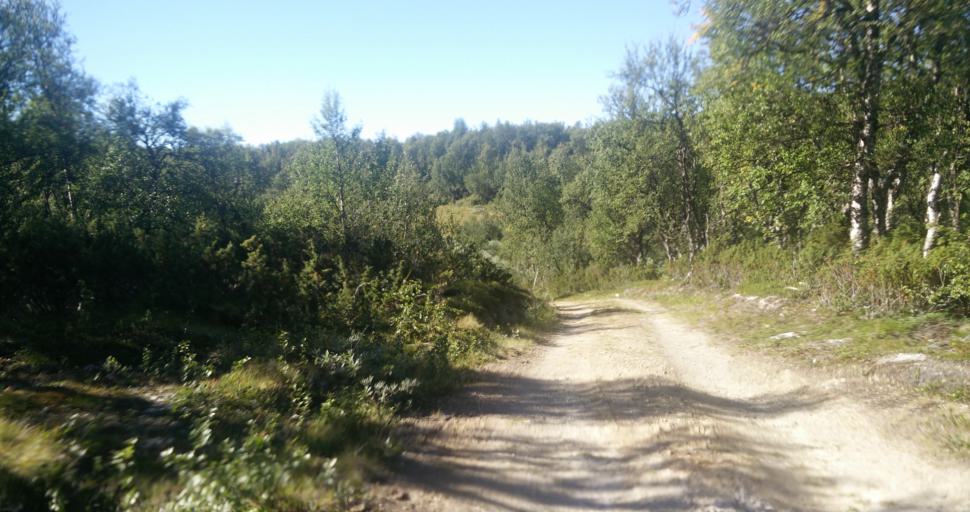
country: NO
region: Sor-Trondelag
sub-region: Tydal
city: Aas
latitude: 62.7134
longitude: 12.4628
